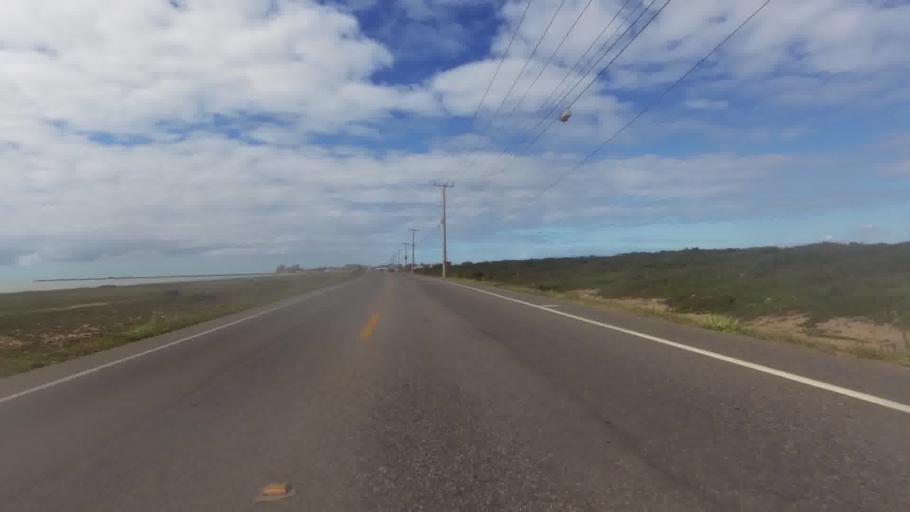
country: BR
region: Espirito Santo
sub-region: Itapemirim
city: Itapemirim
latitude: -20.9923
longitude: -40.8108
